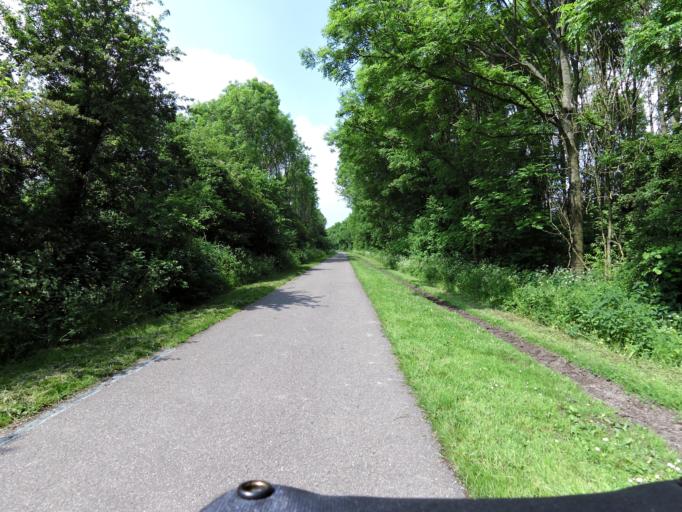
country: NL
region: South Holland
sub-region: Gemeente Spijkenisse
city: Spijkenisse
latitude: 51.8141
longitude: 4.2918
